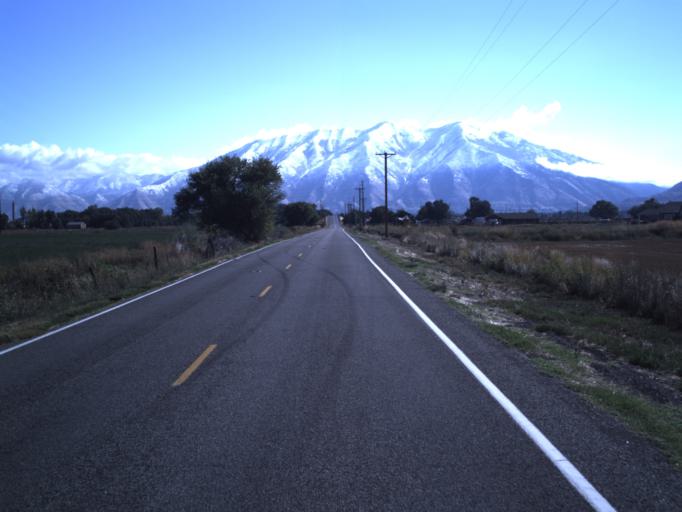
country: US
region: Utah
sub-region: Utah County
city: Benjamin
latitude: 40.0983
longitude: -111.7015
